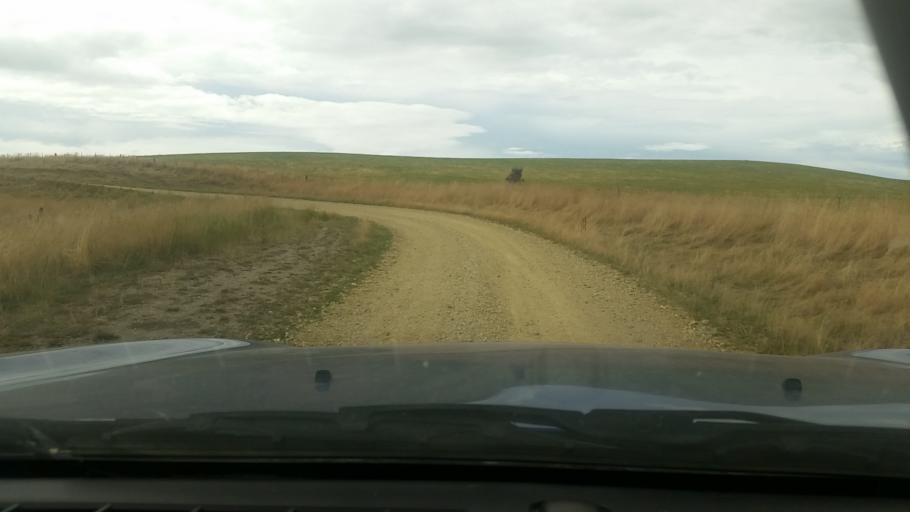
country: NZ
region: Southland
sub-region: Gore District
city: Gore
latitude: -45.5810
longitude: 169.4053
